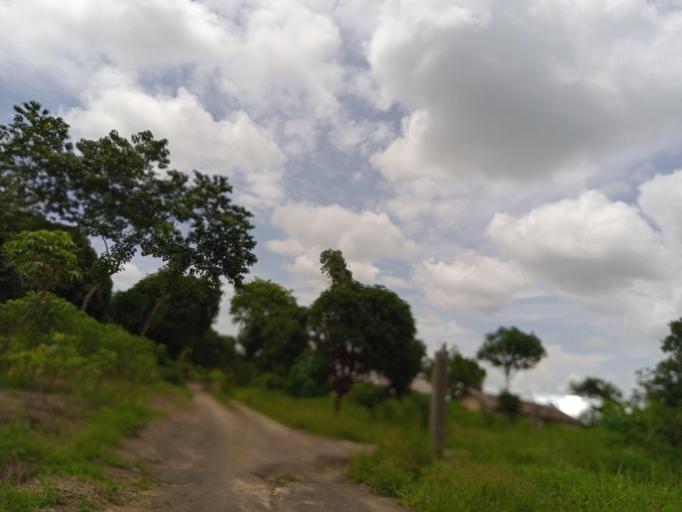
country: SL
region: Northern Province
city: Masoyila
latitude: 8.5923
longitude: -13.1826
